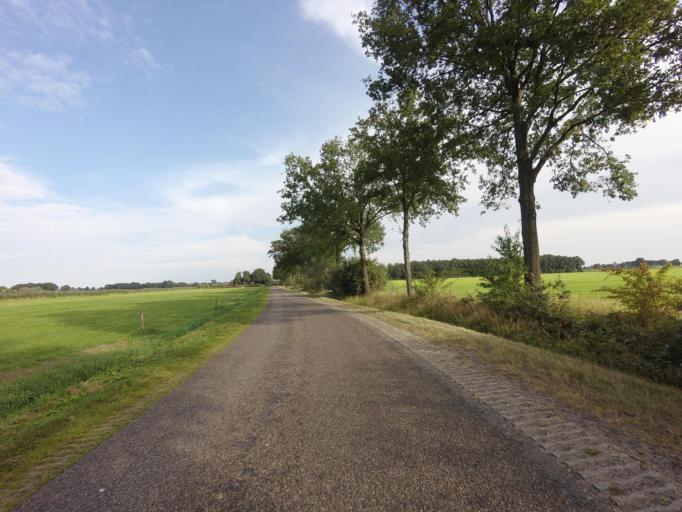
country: DE
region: Lower Saxony
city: Wielen
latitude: 52.5752
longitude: 6.6801
